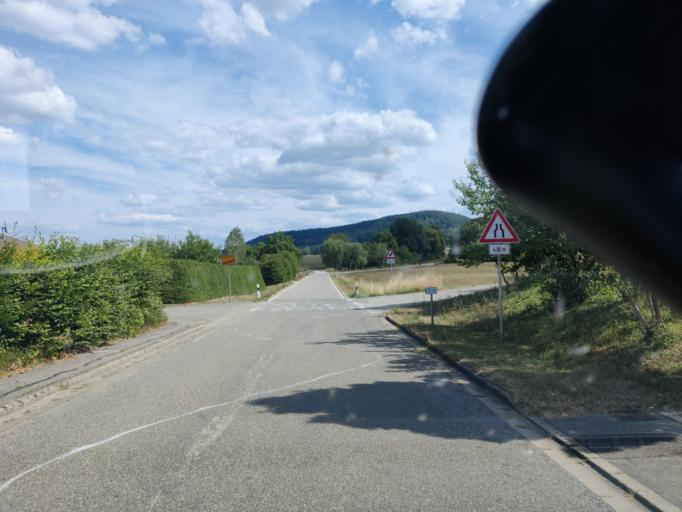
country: DE
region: Bavaria
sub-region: Regierungsbezirk Mittelfranken
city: Bergen
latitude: 49.0987
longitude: 11.1376
